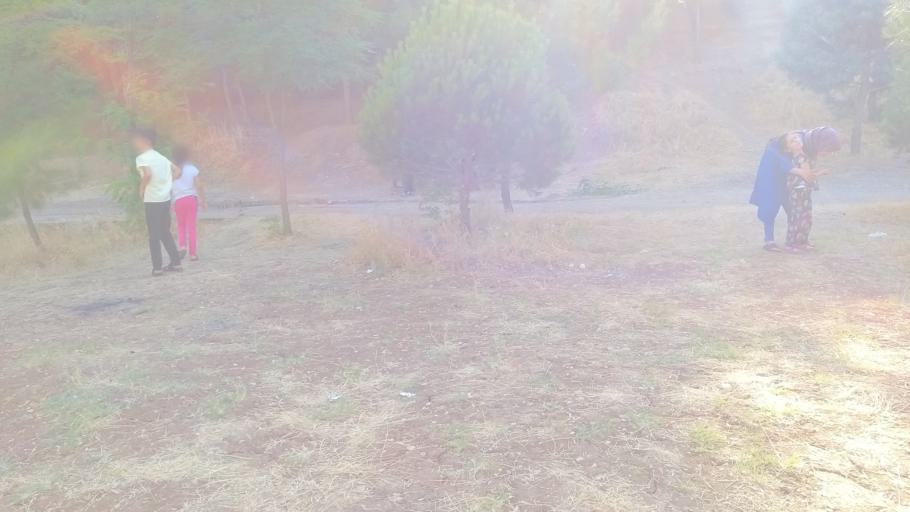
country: TR
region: Diyarbakir
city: Malabadi
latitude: 38.1559
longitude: 41.2019
